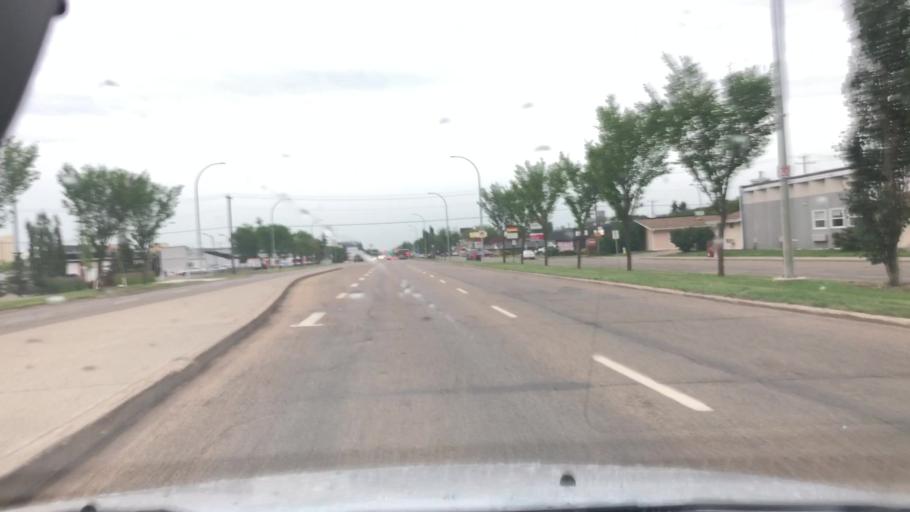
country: CA
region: Alberta
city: St. Albert
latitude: 53.5589
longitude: -113.5858
